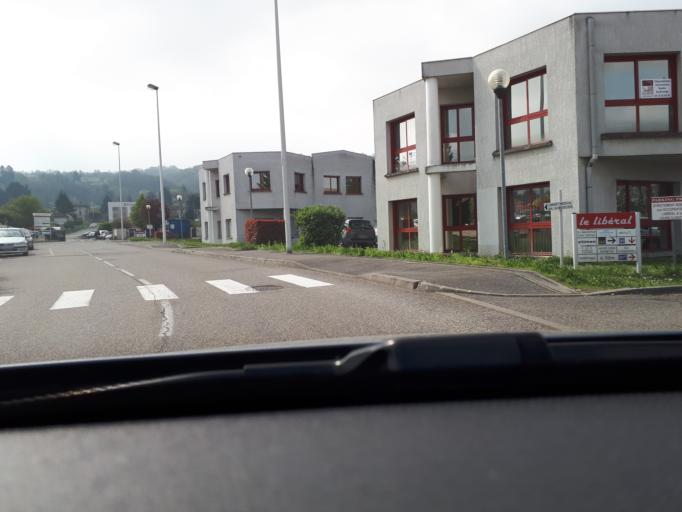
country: FR
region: Rhone-Alpes
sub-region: Departement de l'Isere
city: Bourgoin-Jallieu
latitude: 45.5883
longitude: 5.2607
